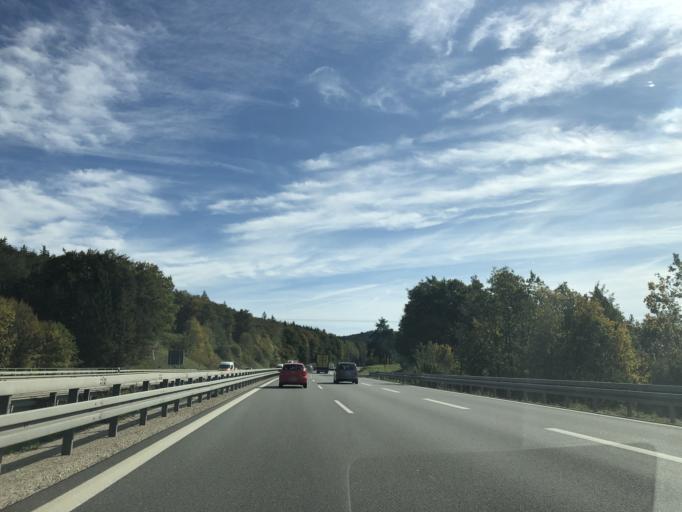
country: DE
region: Bavaria
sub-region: Upper Palatinate
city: Velburg
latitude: 49.2246
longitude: 11.6440
